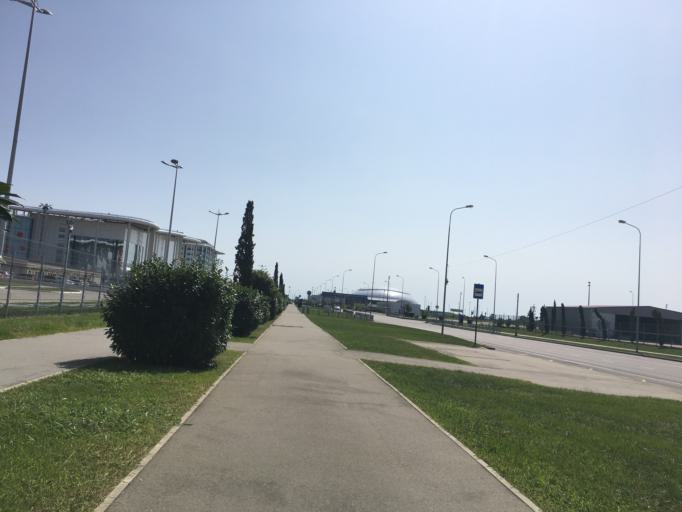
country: RU
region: Krasnodarskiy
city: Adler
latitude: 43.4151
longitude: 39.9479
